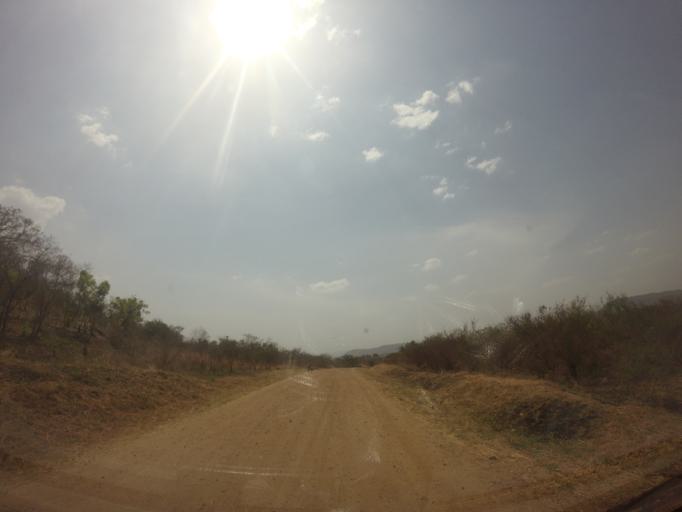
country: UG
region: Northern Region
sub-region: Arua District
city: Arua
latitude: 2.9089
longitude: 31.0613
